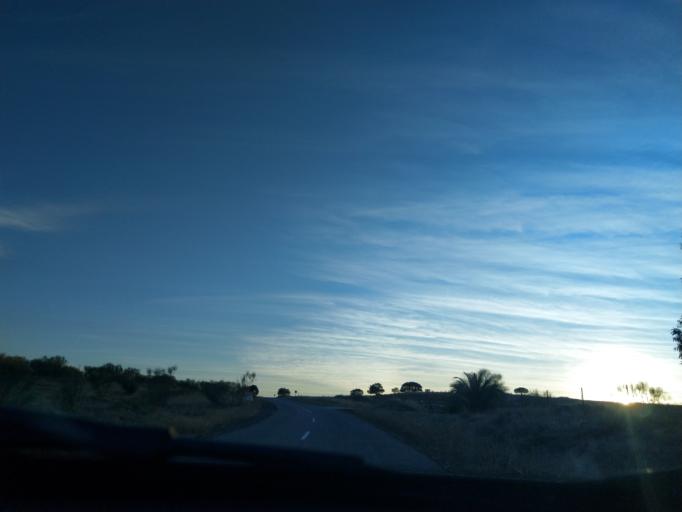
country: ES
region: Extremadura
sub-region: Provincia de Badajoz
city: Valverde de Llerena
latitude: 38.1974
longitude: -5.8512
